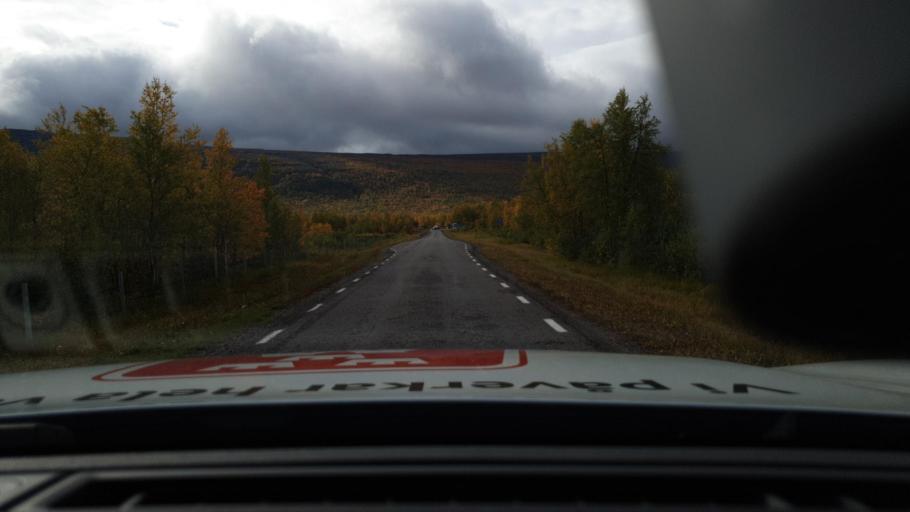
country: SE
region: Norrbotten
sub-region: Kiruna Kommun
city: Kiruna
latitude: 67.8538
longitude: 19.0195
